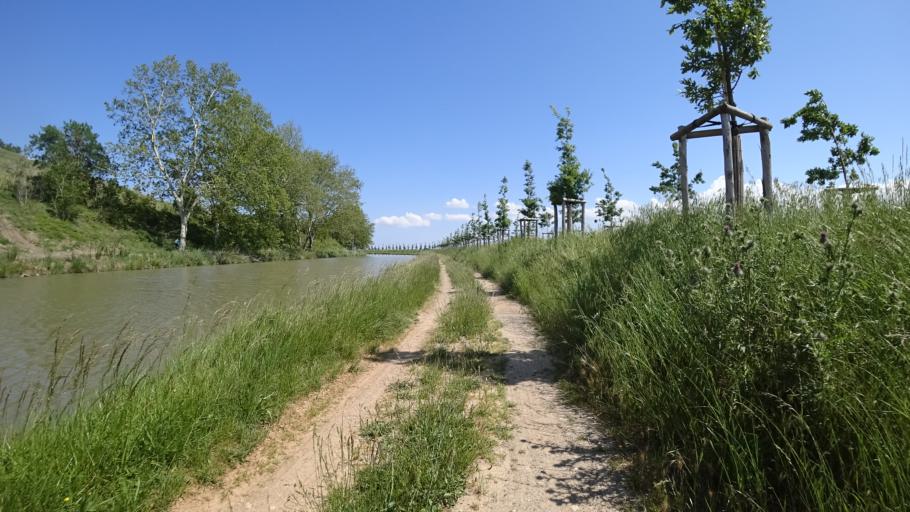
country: FR
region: Languedoc-Roussillon
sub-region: Departement de l'Aude
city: Canet
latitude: 43.2495
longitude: 2.8436
